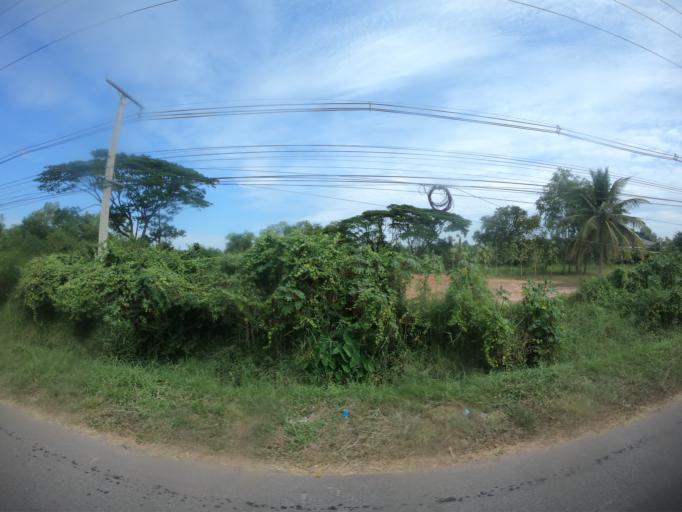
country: TH
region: Maha Sarakham
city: Chiang Yuen
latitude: 16.4128
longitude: 103.0908
